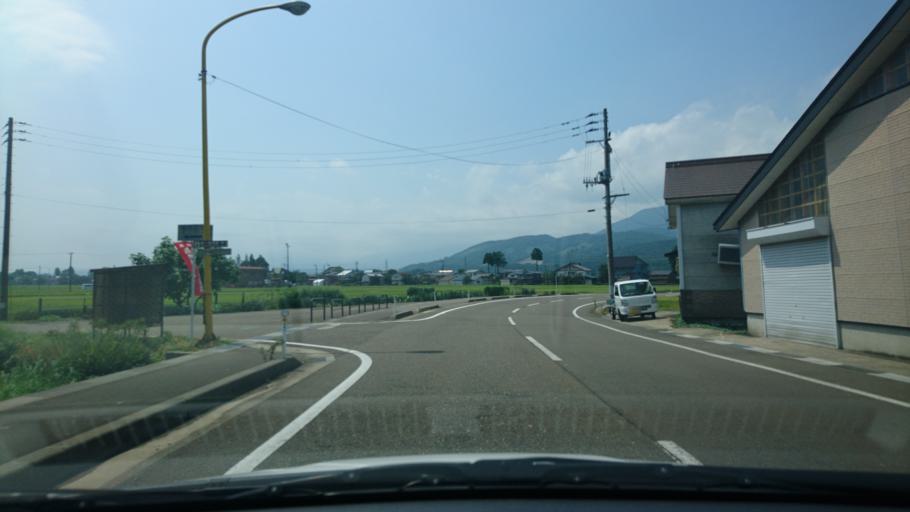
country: JP
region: Niigata
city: Arai
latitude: 37.0517
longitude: 138.2519
